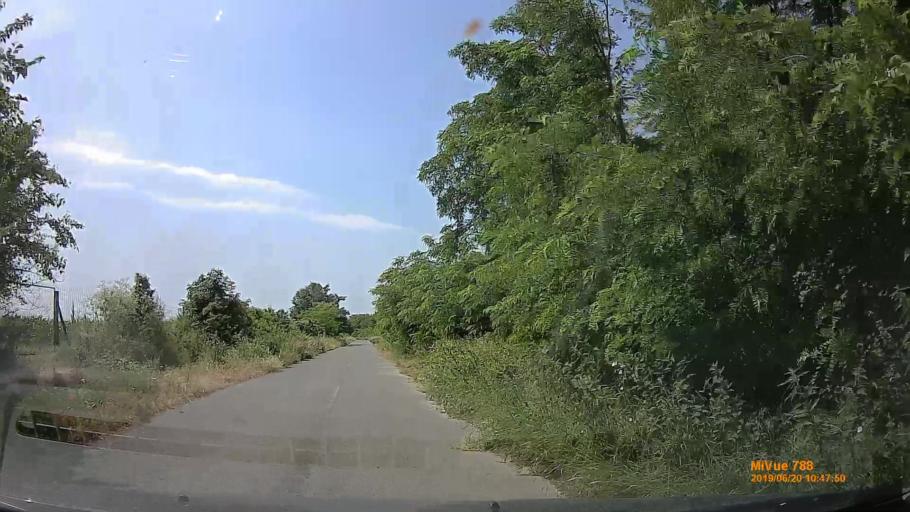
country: HU
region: Baranya
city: Hidas
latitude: 46.1737
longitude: 18.5825
